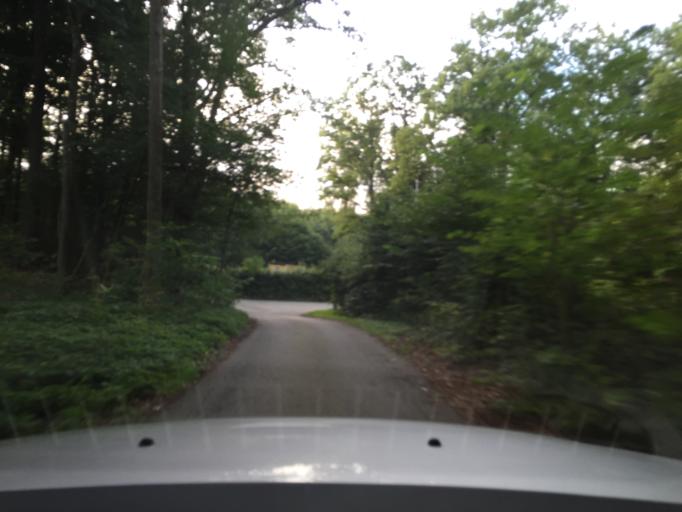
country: SE
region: Skane
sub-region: Hassleholms Kommun
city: Sosdala
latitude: 56.0008
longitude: 13.6372
